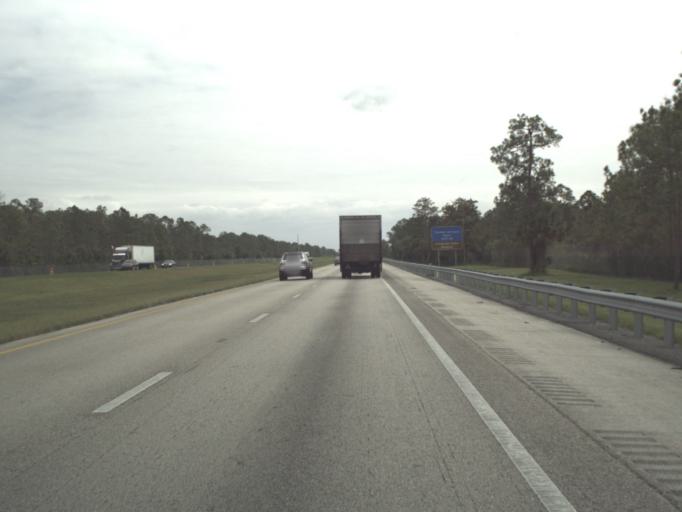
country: US
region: Florida
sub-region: Collier County
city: Orangetree
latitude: 26.1530
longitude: -81.4748
